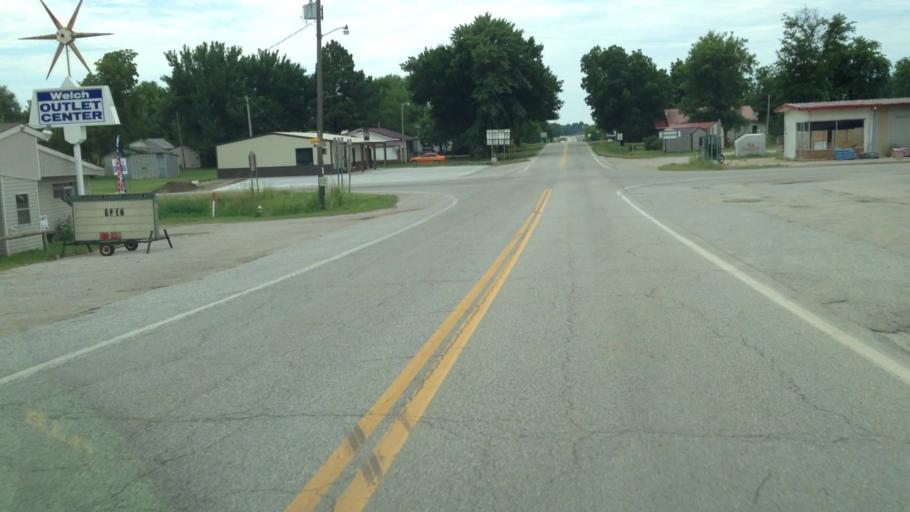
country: US
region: Kansas
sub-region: Labette County
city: Chetopa
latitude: 36.8732
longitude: -95.0989
